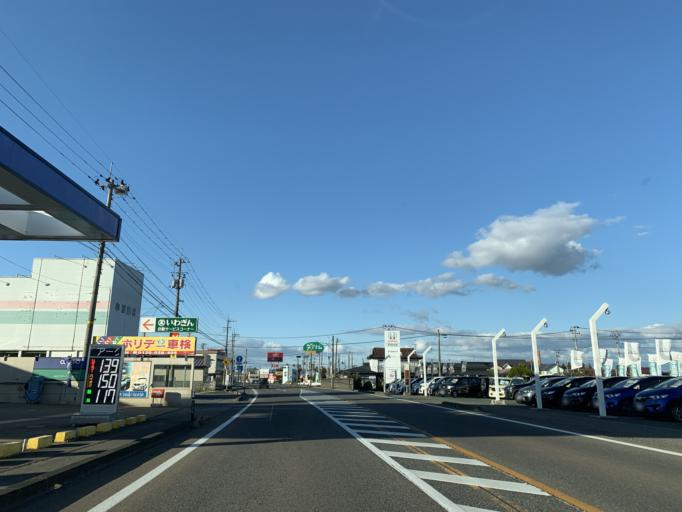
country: JP
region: Iwate
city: Mizusawa
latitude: 39.1640
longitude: 141.1440
